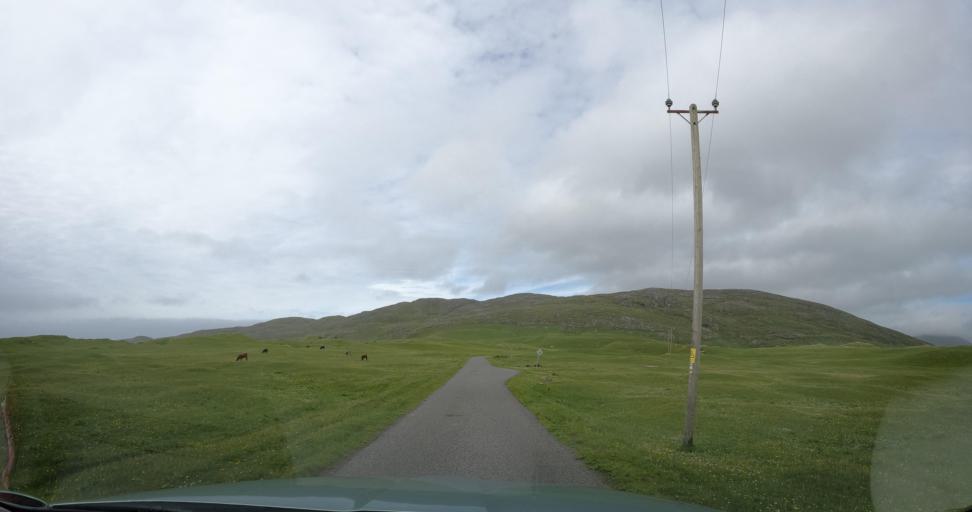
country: GB
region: Scotland
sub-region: Eilean Siar
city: Barra
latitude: 56.9224
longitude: -7.5385
